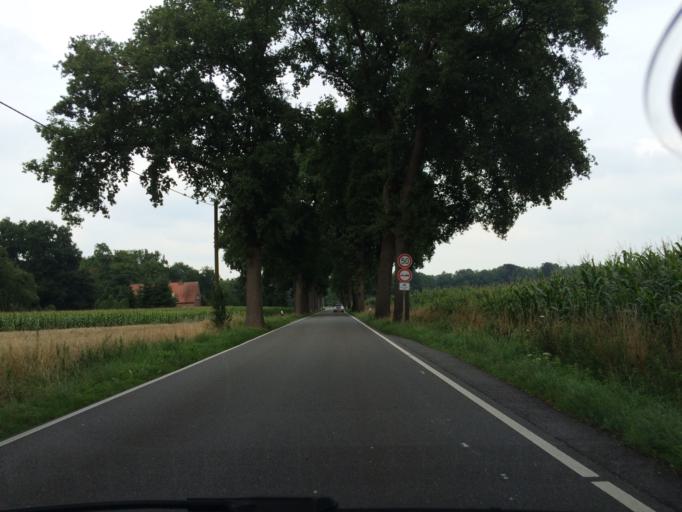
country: DE
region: North Rhine-Westphalia
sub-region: Regierungsbezirk Munster
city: Klein Reken
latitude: 51.7293
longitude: 7.0010
